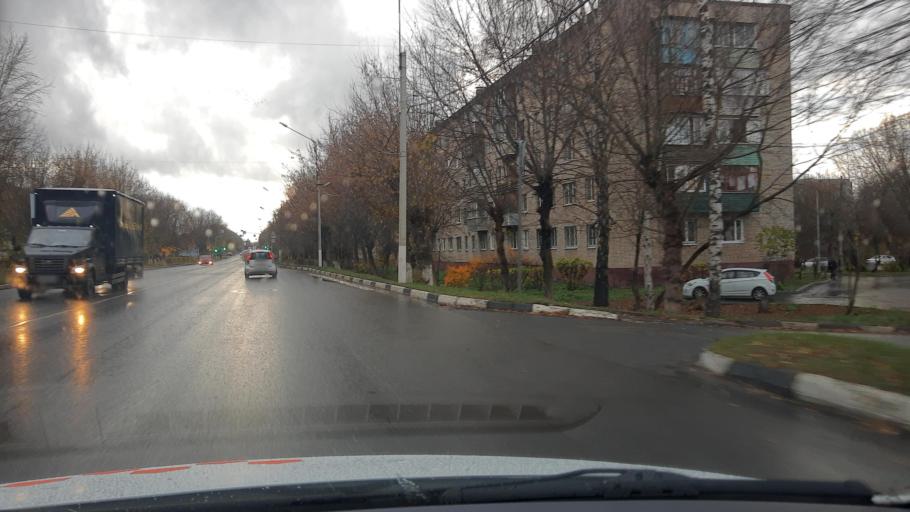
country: RU
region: Moskovskaya
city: Noginsk
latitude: 55.8412
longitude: 38.4003
